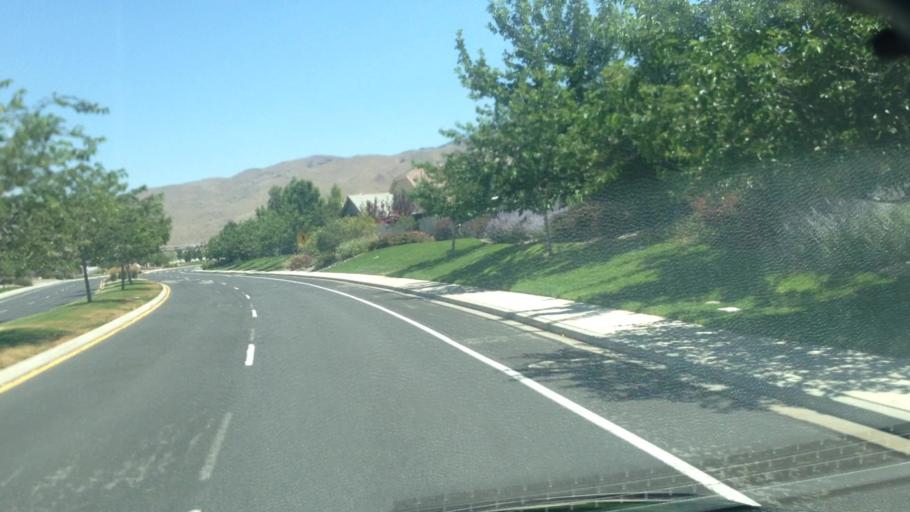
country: US
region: Nevada
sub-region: Washoe County
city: Sparks
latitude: 39.4155
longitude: -119.7251
